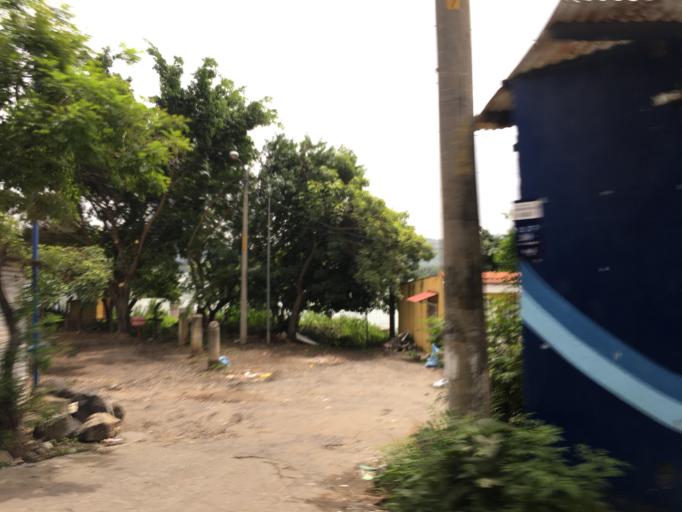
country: GT
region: Guatemala
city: Villa Canales
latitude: 14.4549
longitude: -90.5719
